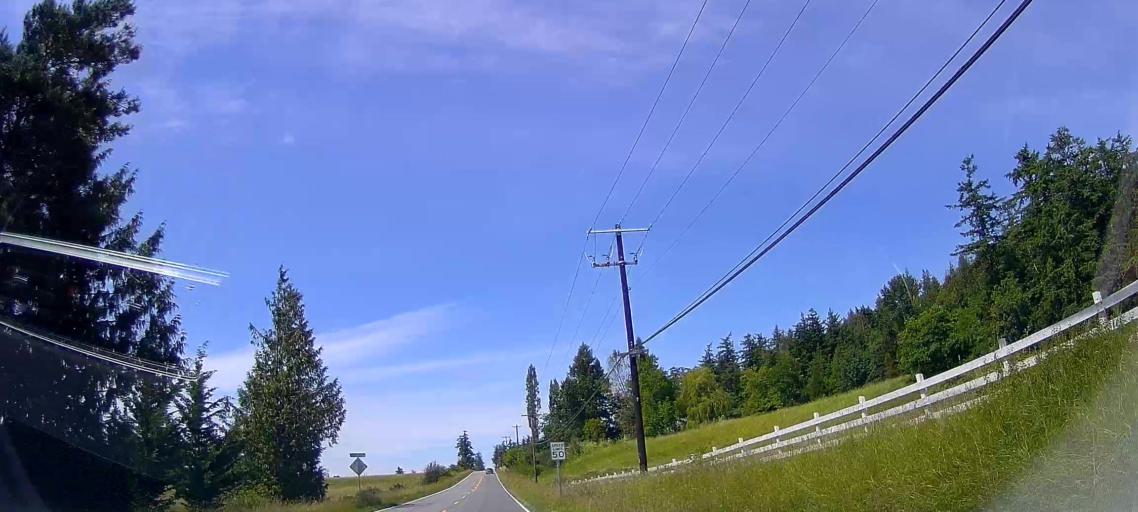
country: US
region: Washington
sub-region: Snohomish County
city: Stanwood
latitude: 48.2582
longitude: -122.3566
